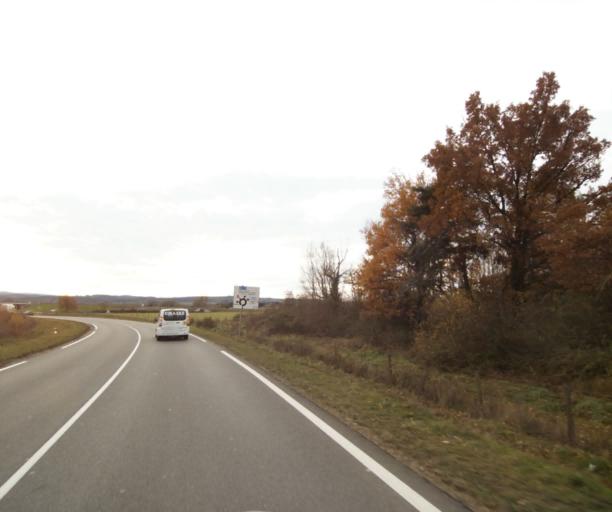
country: FR
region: Rhone-Alpes
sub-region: Departement de la Loire
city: Sury-le-Comtal
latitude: 45.5146
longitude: 4.1901
